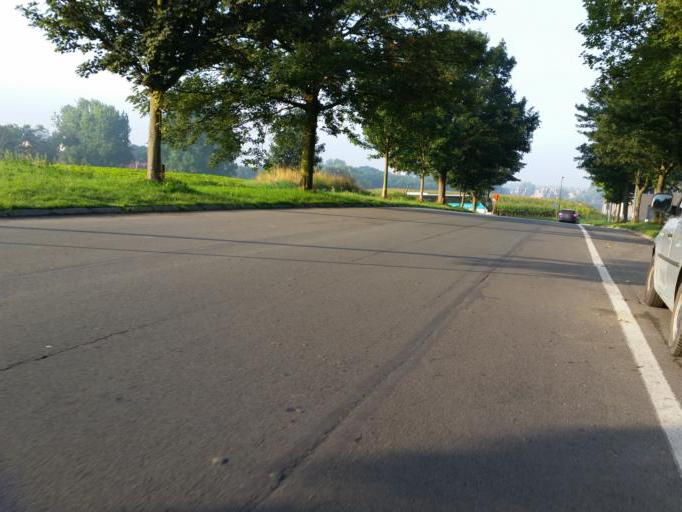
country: BE
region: Flanders
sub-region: Provincie Vlaams-Brabant
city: Grimbergen
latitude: 50.9038
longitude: 4.3807
